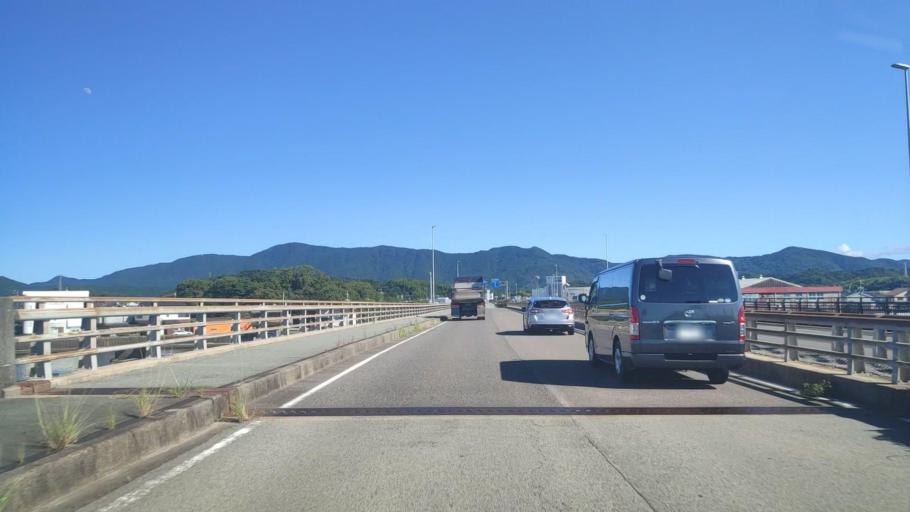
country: JP
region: Mie
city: Ise
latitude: 34.5029
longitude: 136.7379
